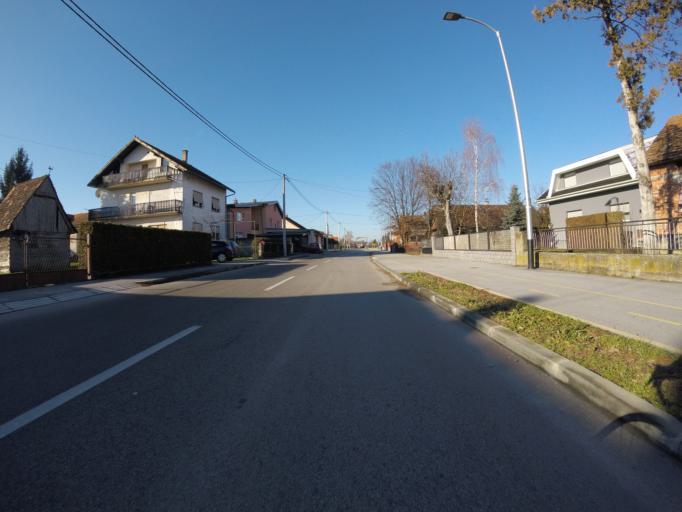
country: HR
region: Zagrebacka
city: Gradici
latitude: 45.7002
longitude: 16.0644
